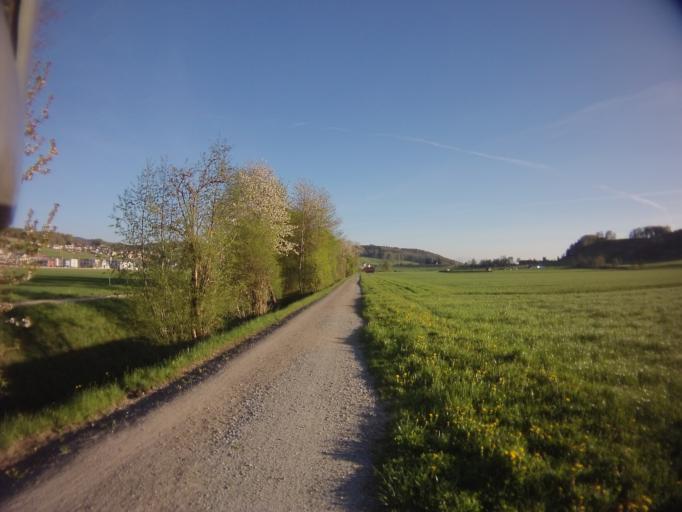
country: CH
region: Zurich
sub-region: Bezirk Affoltern
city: Schachen
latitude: 47.3279
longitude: 8.4654
